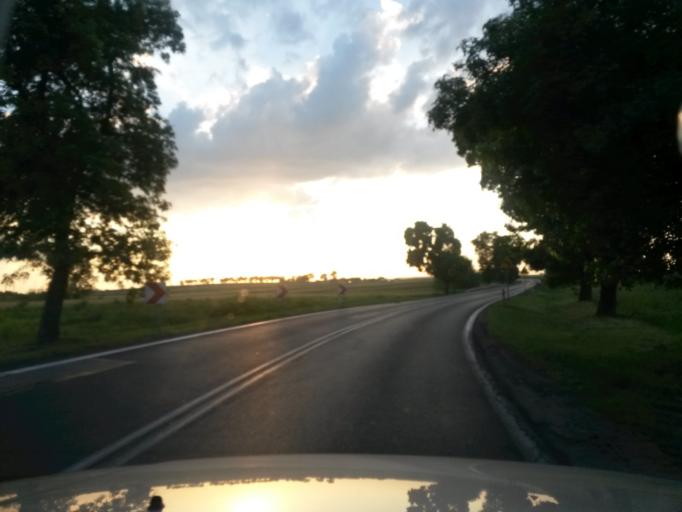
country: PL
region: Lodz Voivodeship
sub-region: Powiat wielunski
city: Wielun
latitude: 51.2454
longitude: 18.5225
